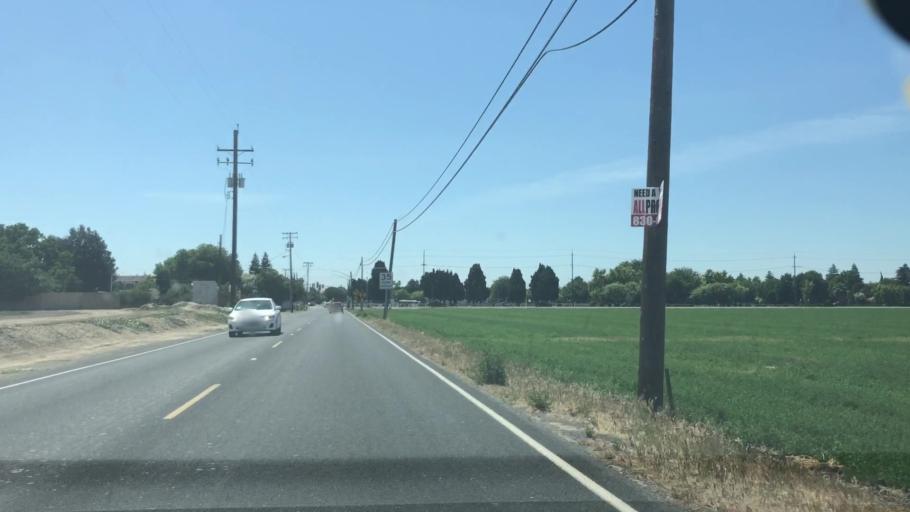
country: US
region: California
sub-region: San Joaquin County
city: Tracy
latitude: 37.7252
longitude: -121.4135
